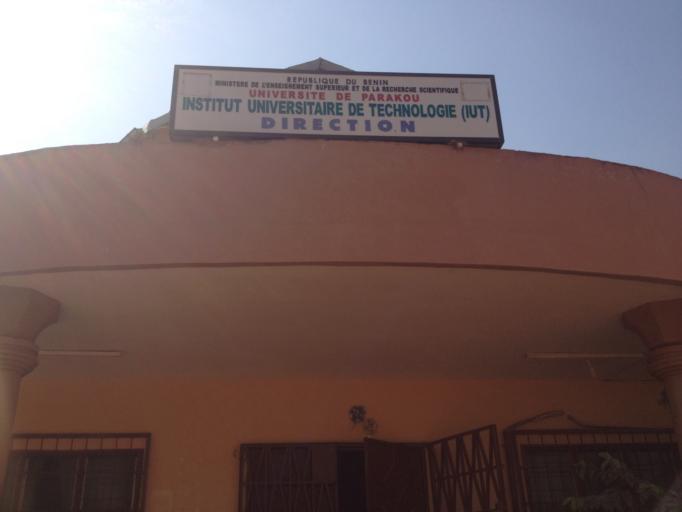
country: BJ
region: Borgou
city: Parakou
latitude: 9.3381
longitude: 2.6452
